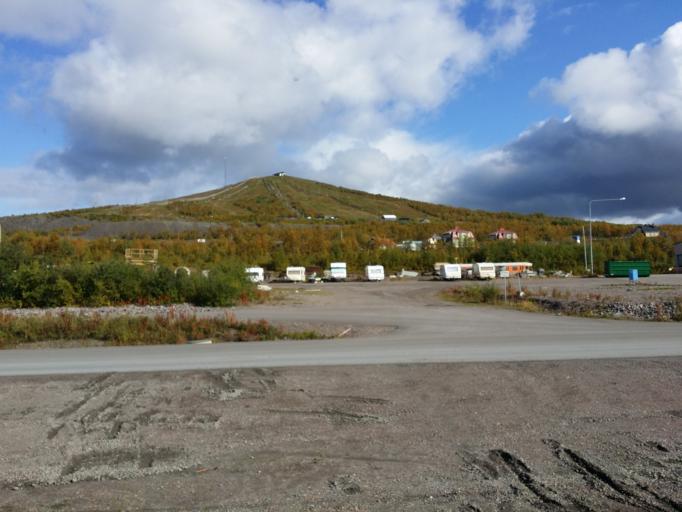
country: SE
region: Norrbotten
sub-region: Kiruna Kommun
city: Kiruna
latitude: 67.8700
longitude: 20.1974
